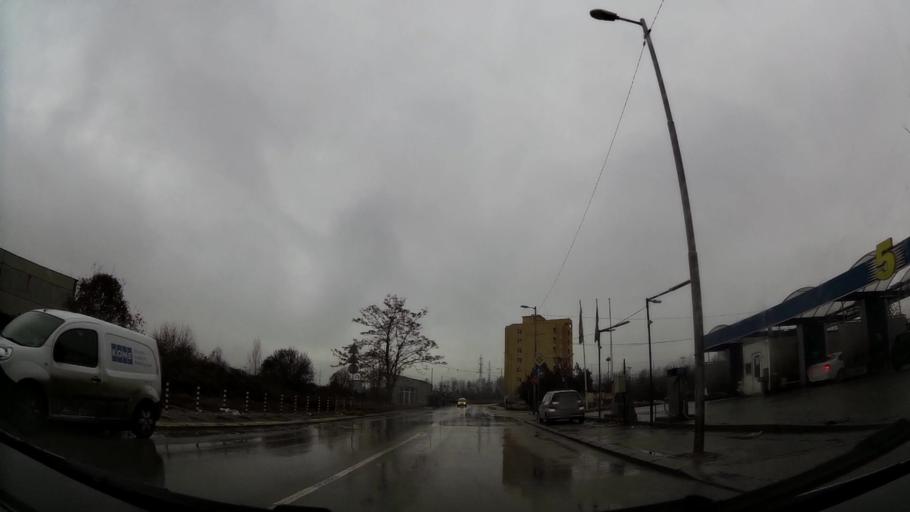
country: BG
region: Sofia-Capital
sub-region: Stolichna Obshtina
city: Sofia
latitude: 42.6260
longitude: 23.3847
